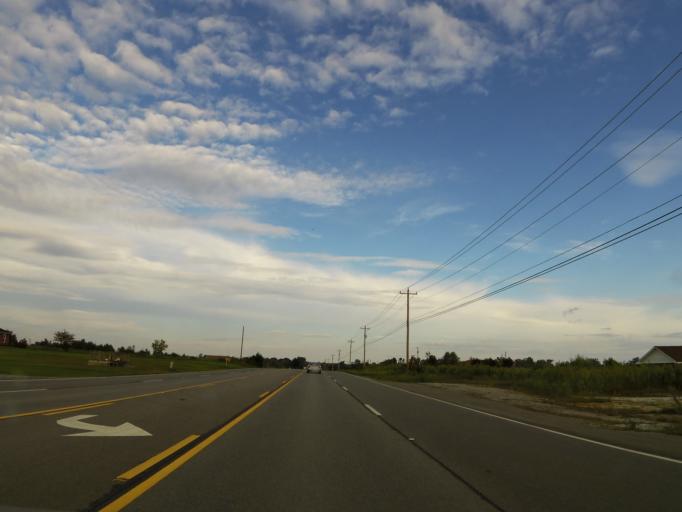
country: US
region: Alabama
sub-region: Lauderdale County
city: Rogersville
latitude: 34.7992
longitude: -87.1387
